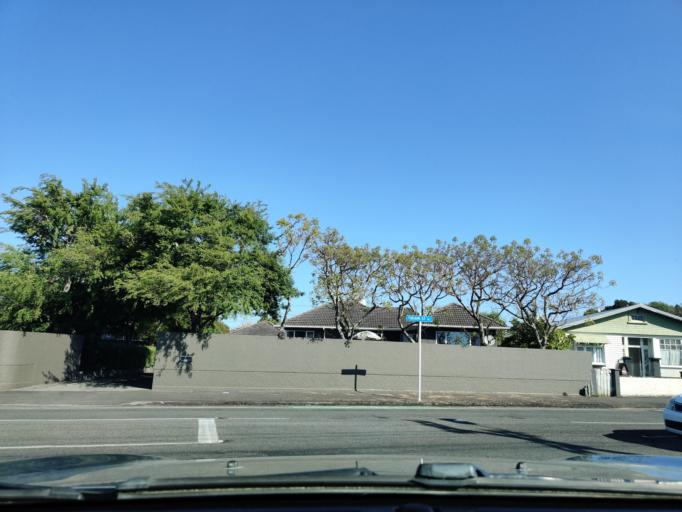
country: NZ
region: Taranaki
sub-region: New Plymouth District
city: New Plymouth
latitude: -39.0739
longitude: 174.0587
